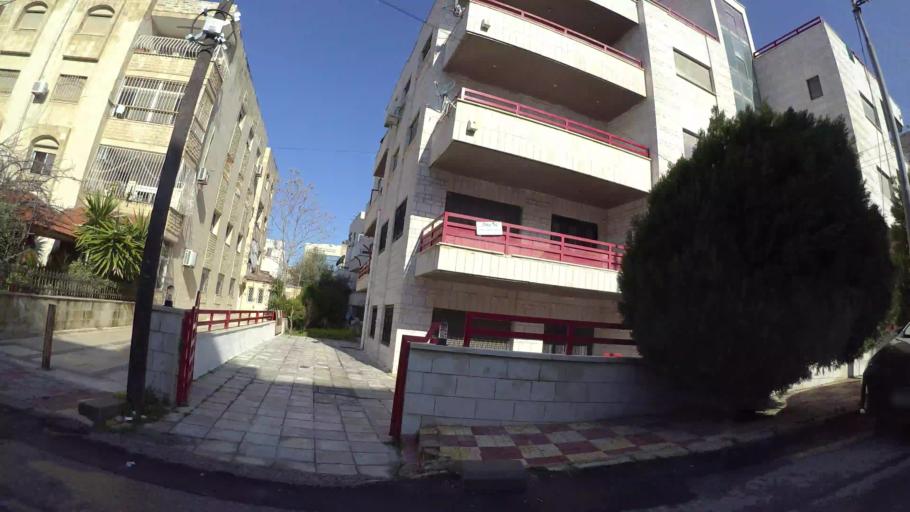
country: JO
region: Amman
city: Al Jubayhah
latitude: 32.0014
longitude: 35.8790
